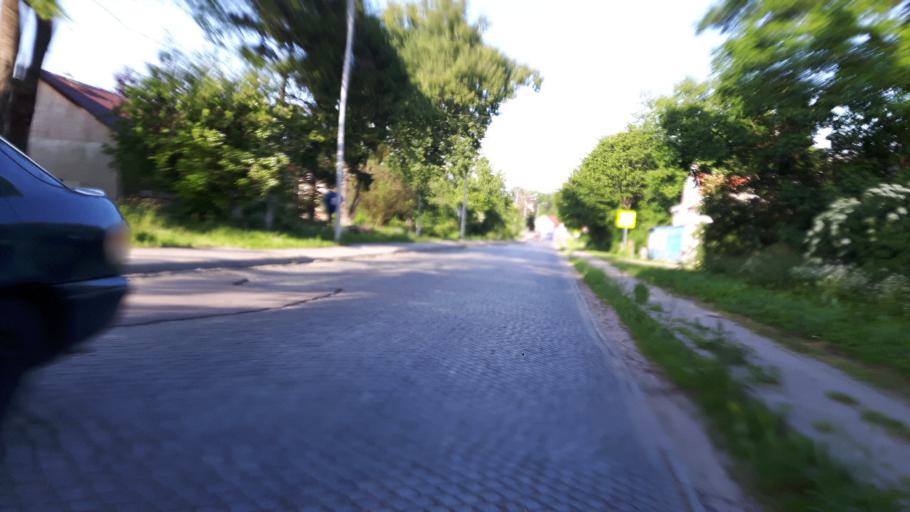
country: RU
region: Kaliningrad
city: Ladushkin
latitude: 54.5009
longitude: 20.0914
